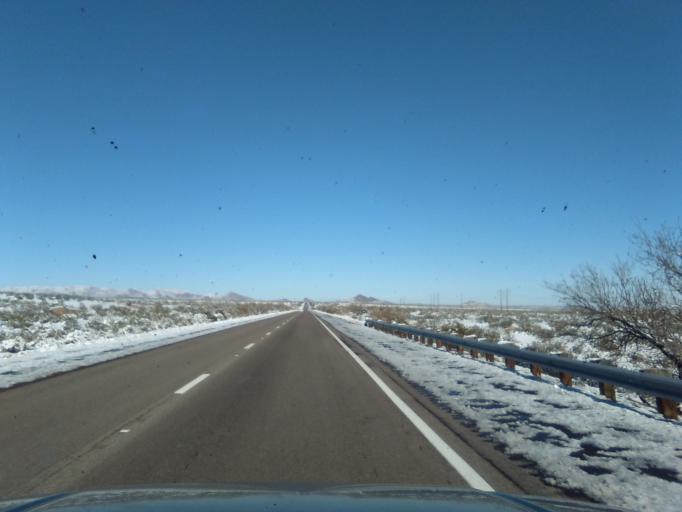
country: US
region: New Mexico
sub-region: Socorro County
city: Socorro
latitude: 33.6926
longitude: -107.0580
